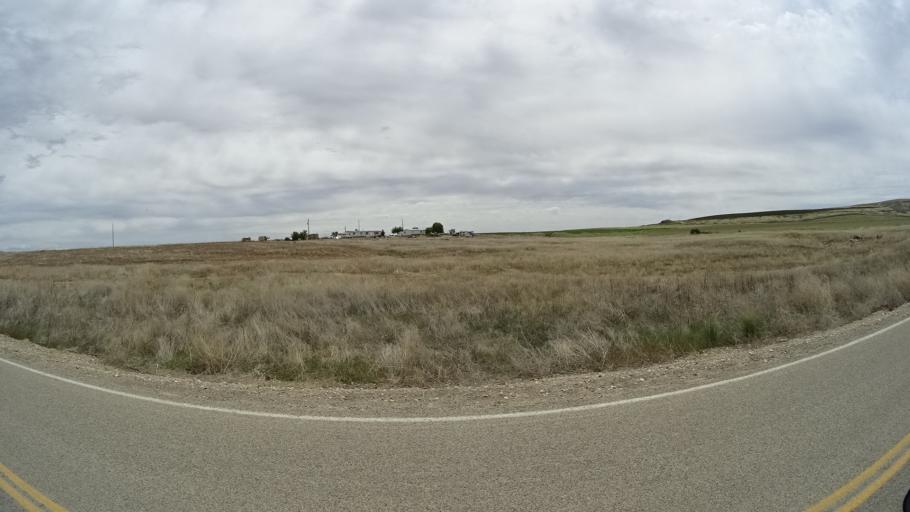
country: US
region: Idaho
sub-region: Ada County
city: Kuna
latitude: 43.4716
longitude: -116.4361
